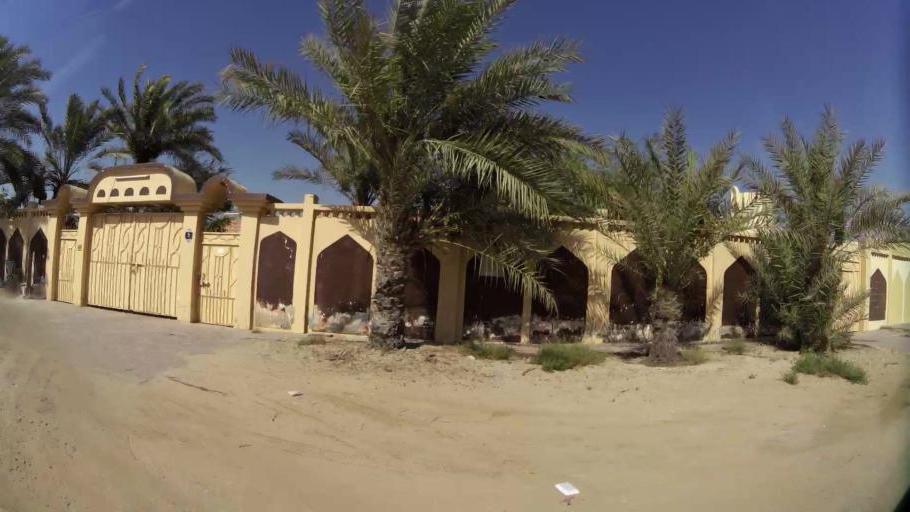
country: AE
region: Ajman
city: Ajman
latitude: 25.4141
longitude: 55.4680
